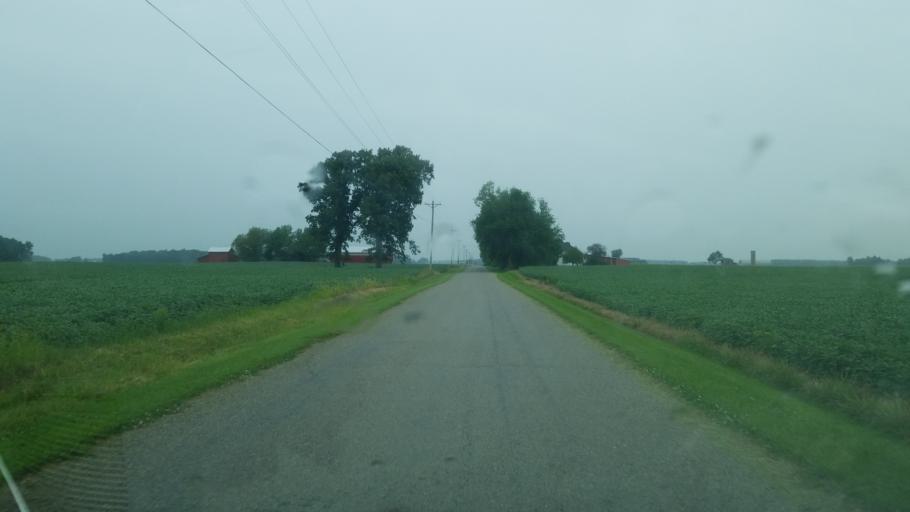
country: US
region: Ohio
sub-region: Huron County
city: Willard
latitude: 41.0022
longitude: -82.8137
